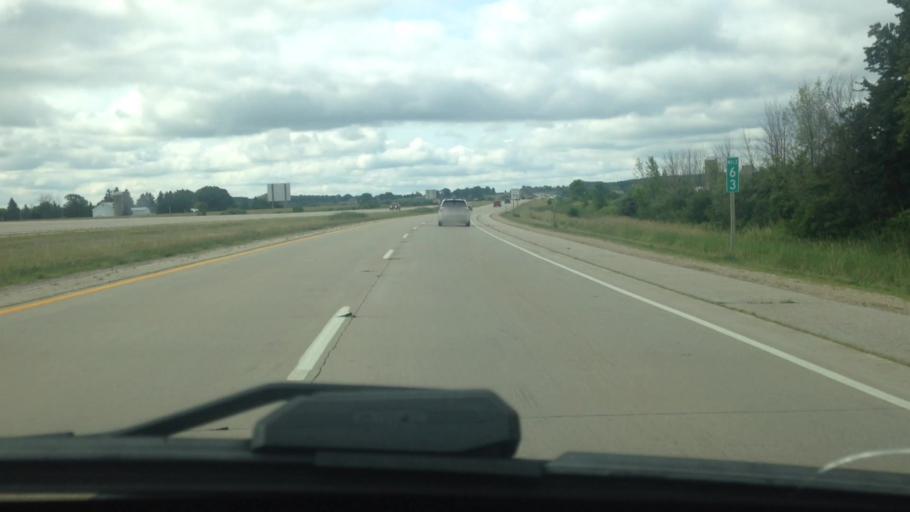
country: US
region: Wisconsin
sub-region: Washington County
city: Jackson
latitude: 43.3158
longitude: -88.1844
